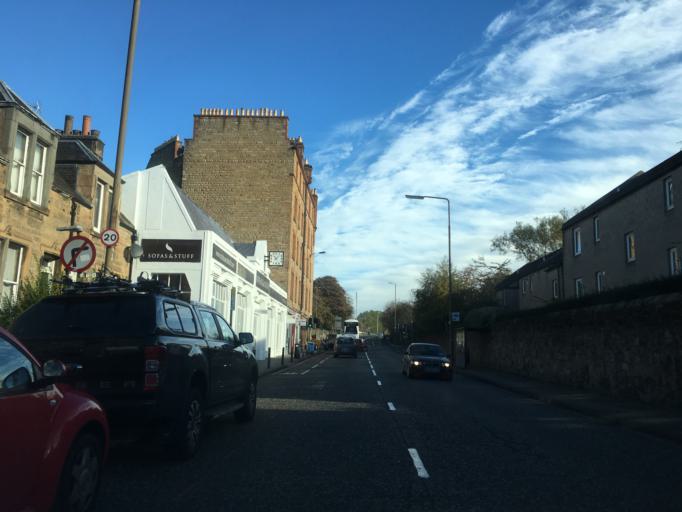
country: GB
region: Scotland
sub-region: Edinburgh
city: Edinburgh
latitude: 55.9384
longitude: -3.2244
